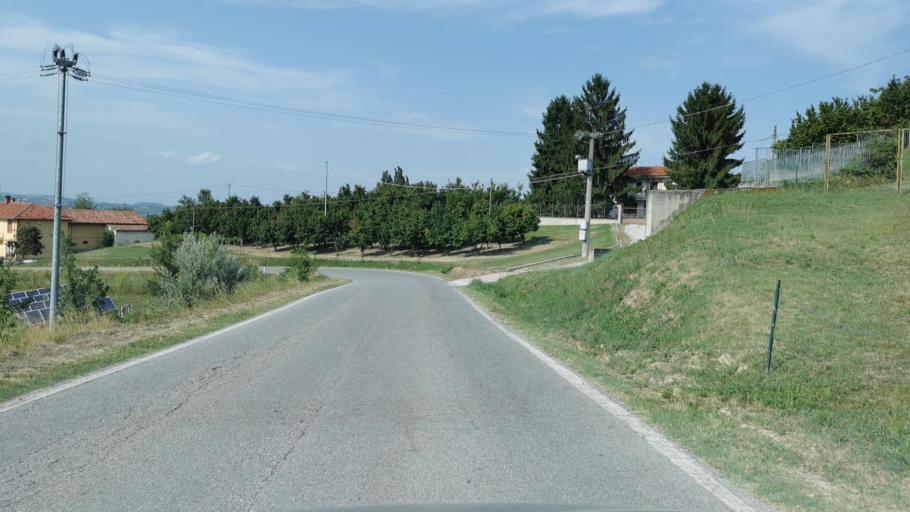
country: IT
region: Piedmont
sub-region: Provincia di Cuneo
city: La Morra
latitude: 44.6479
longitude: 7.8992
